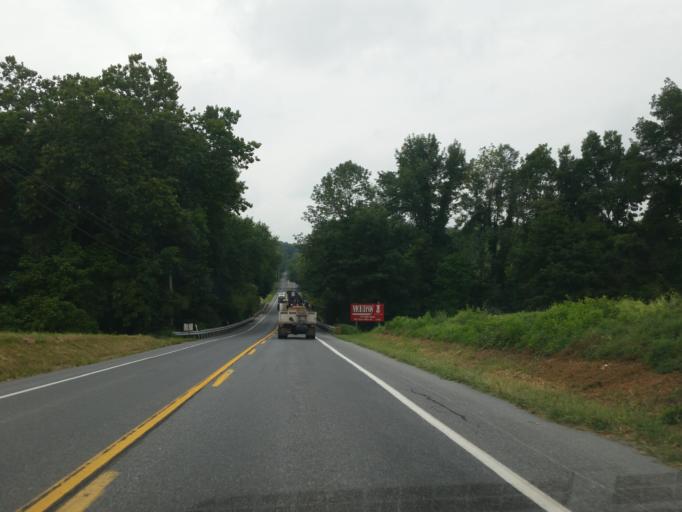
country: US
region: Pennsylvania
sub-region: Lancaster County
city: Brickerville
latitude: 40.2001
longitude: -76.3013
